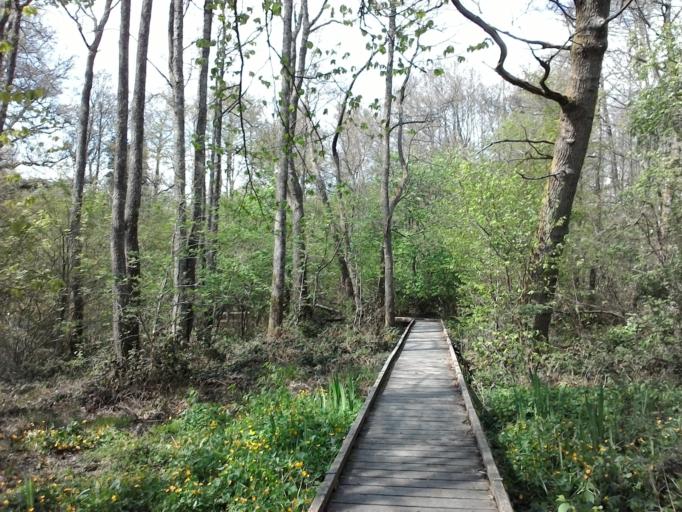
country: FR
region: Bourgogne
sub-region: Departement de la Cote-d'Or
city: Saulieu
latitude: 47.1827
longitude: 4.0764
